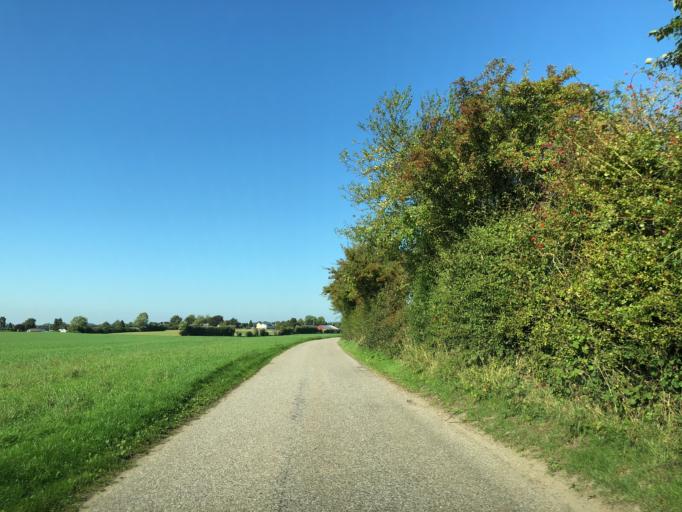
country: DK
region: South Denmark
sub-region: Sonderborg Kommune
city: Dybbol
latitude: 54.9484
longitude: 9.7300
